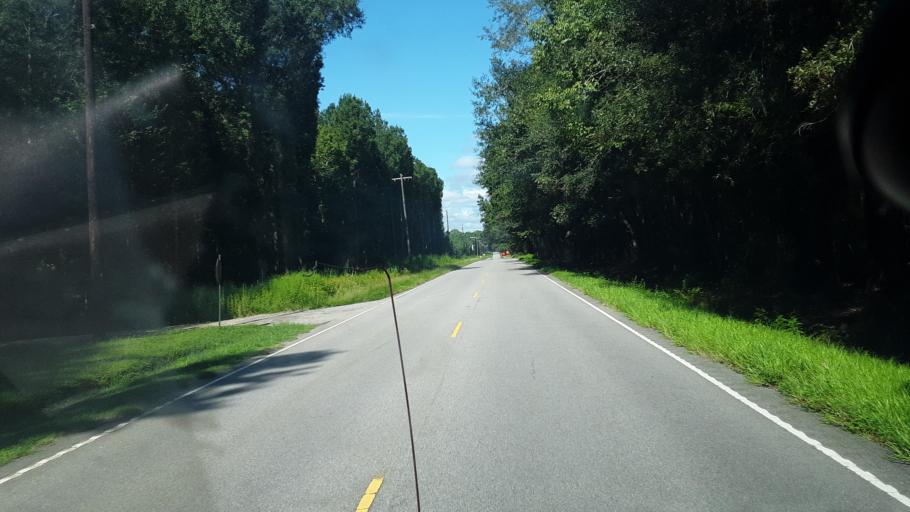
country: US
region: South Carolina
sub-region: Jasper County
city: Ridgeland
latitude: 32.5890
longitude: -80.9355
